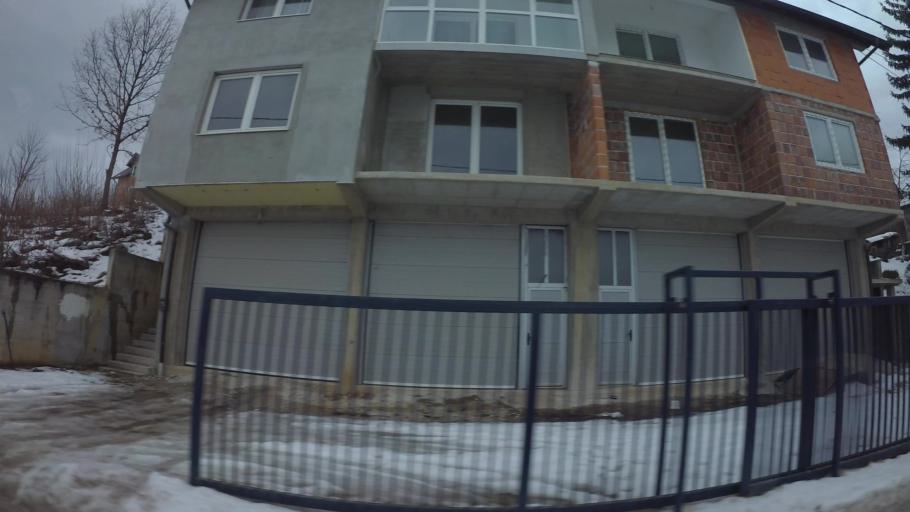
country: BA
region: Federation of Bosnia and Herzegovina
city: Vogosca
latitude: 43.8861
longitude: 18.3167
